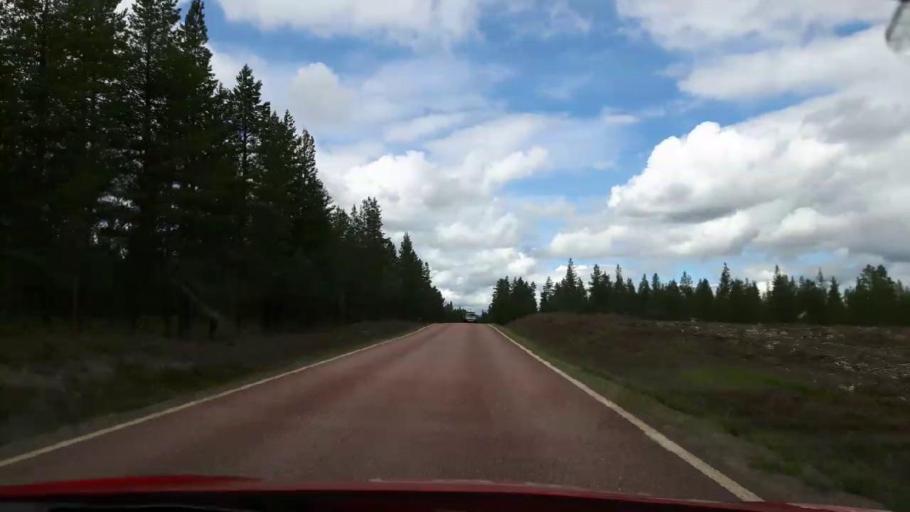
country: NO
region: Hedmark
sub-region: Trysil
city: Innbygda
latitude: 61.8533
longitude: 12.9499
